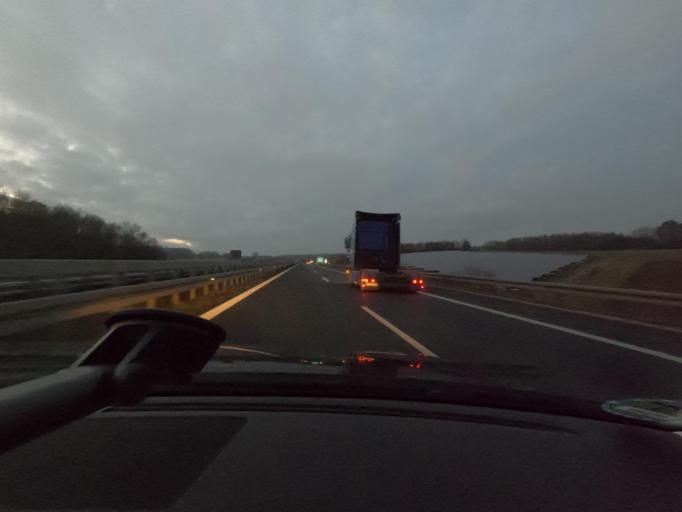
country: DE
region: Bavaria
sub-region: Upper Franconia
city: Lichtenfels
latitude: 50.1579
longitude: 11.0172
